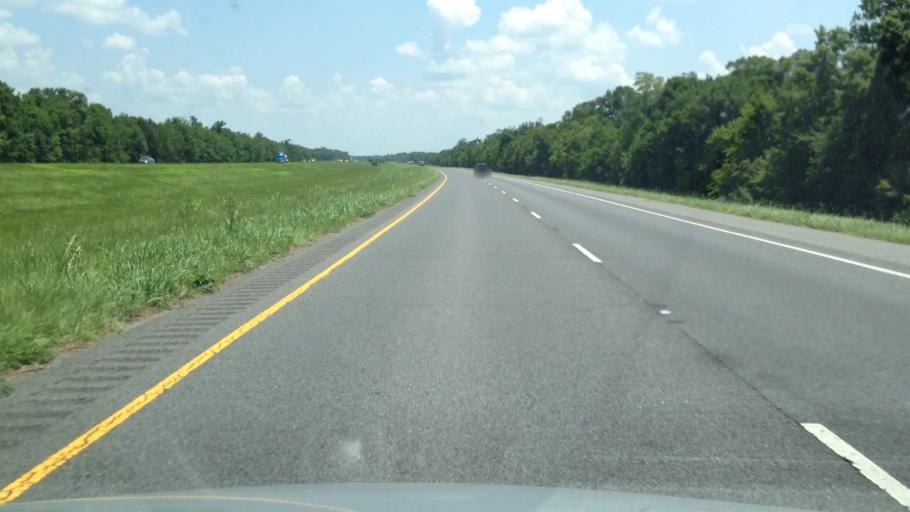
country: US
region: Louisiana
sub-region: Avoyelles Parish
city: Bunkie
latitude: 30.8331
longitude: -92.2279
